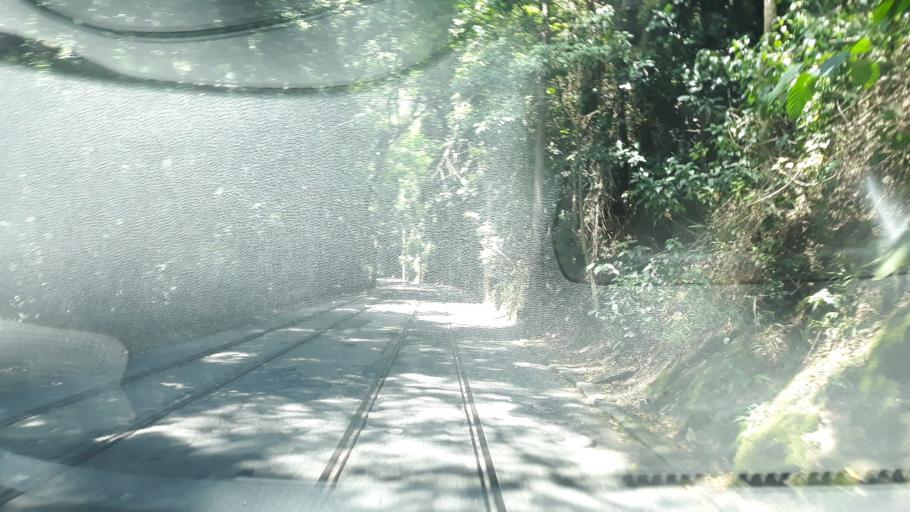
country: BR
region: Rio de Janeiro
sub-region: Rio De Janeiro
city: Rio de Janeiro
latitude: -22.9397
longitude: -43.2099
